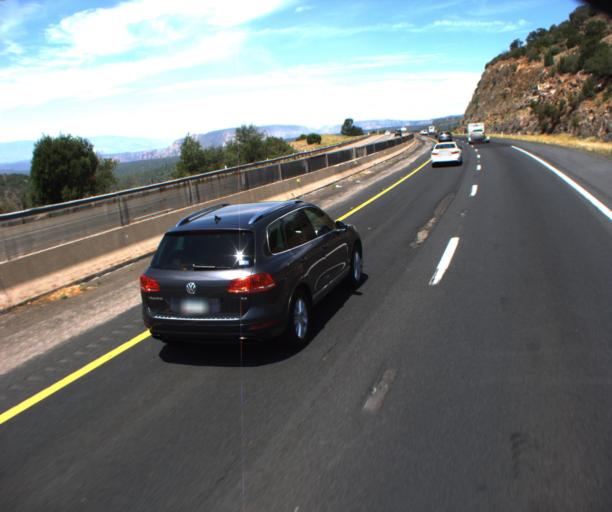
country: US
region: Arizona
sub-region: Yavapai County
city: Village of Oak Creek (Big Park)
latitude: 34.8083
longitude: -111.6011
